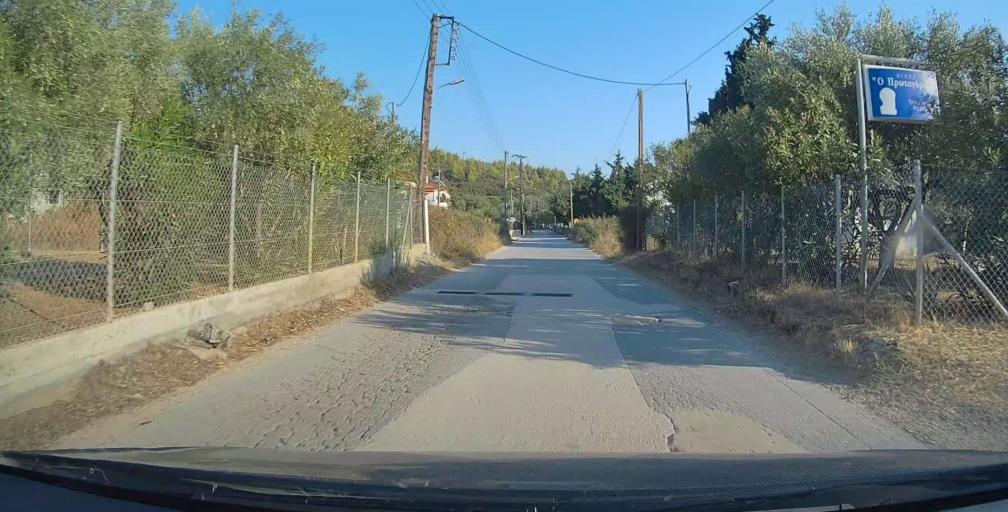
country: GR
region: Central Macedonia
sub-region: Nomos Chalkidikis
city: Sykia
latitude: 39.9961
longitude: 23.8903
